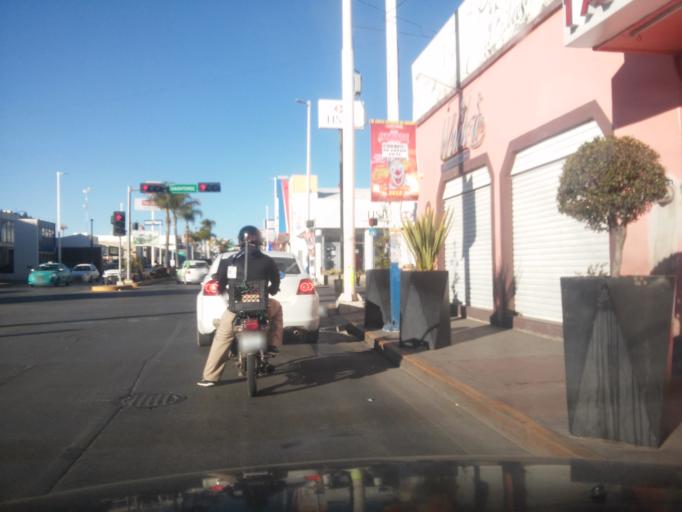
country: MX
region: Durango
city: Victoria de Durango
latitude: 24.0272
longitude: -104.6559
